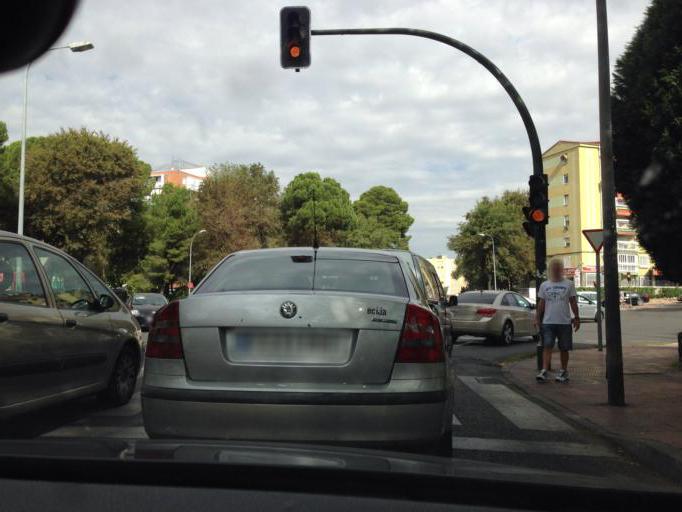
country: ES
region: Madrid
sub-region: Provincia de Madrid
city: Alcala de Henares
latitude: 40.4887
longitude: -3.3743
